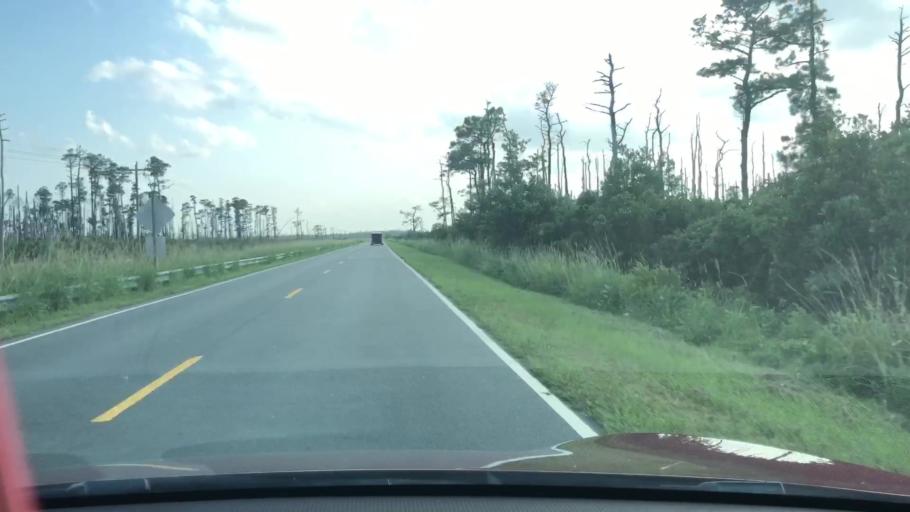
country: US
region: North Carolina
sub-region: Dare County
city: Wanchese
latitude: 35.6293
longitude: -75.7823
